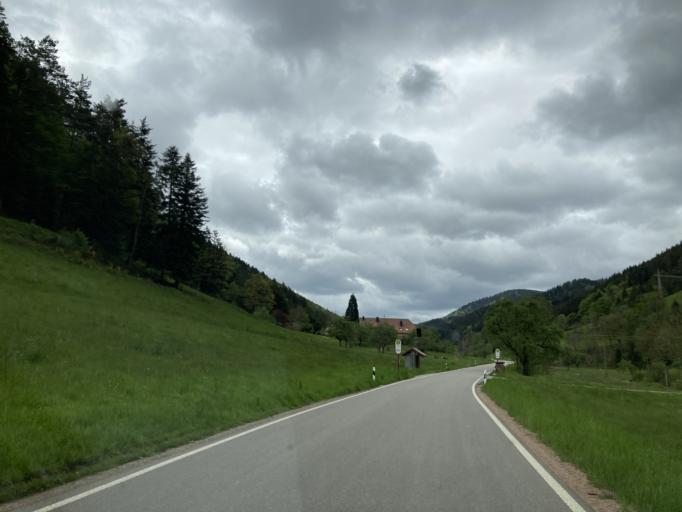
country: DE
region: Baden-Wuerttemberg
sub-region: Freiburg Region
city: Schonach im Schwarzwald
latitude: 48.1966
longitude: 8.1610
